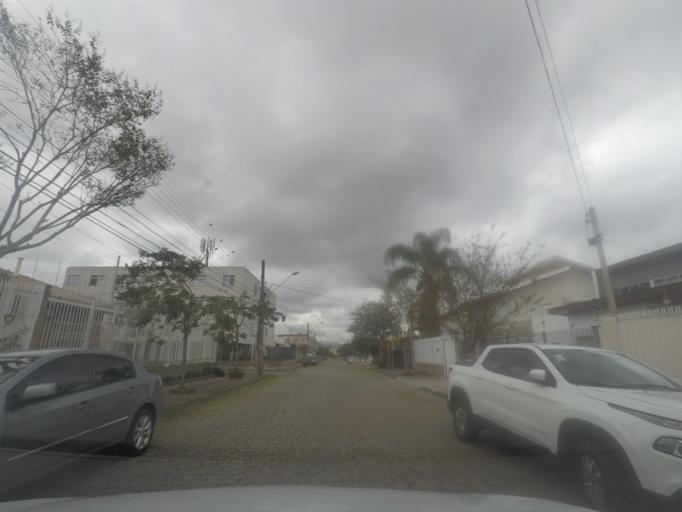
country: BR
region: Parana
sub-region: Curitiba
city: Curitiba
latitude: -25.4408
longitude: -49.2436
